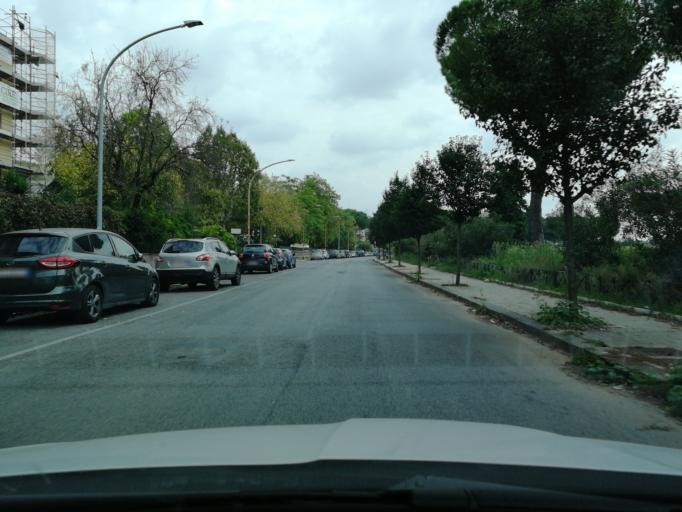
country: IT
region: Latium
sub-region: Citta metropolitana di Roma Capitale
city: Rome
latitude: 41.8554
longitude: 12.5547
